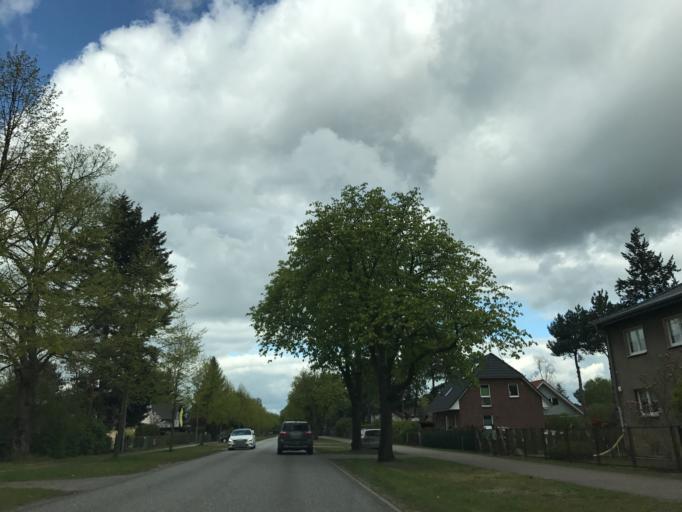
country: DE
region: Brandenburg
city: Brieselang
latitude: 52.5849
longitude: 12.9844
